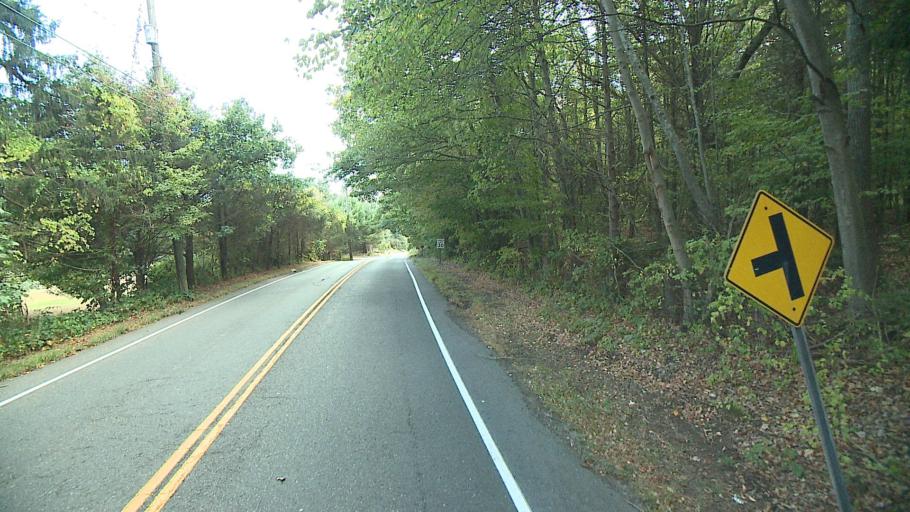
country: US
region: Connecticut
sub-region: New Haven County
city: Oxford
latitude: 41.4328
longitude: -73.0859
